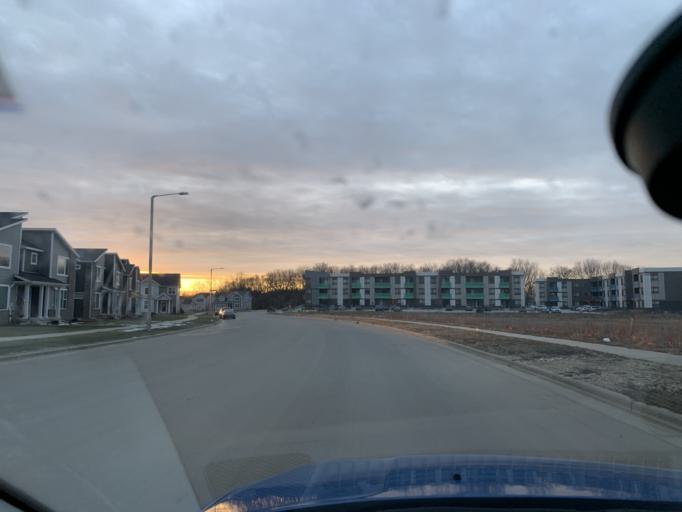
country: US
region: Wisconsin
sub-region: Dane County
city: Verona
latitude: 43.0522
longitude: -89.5570
